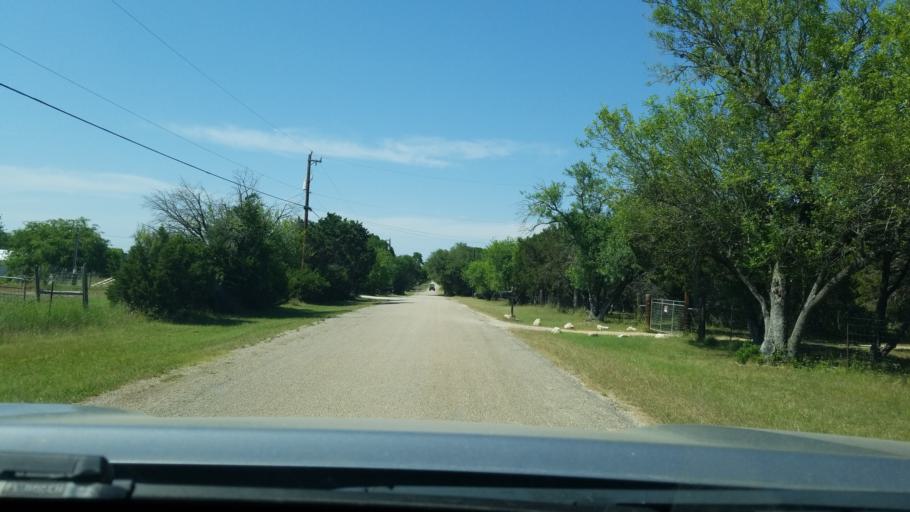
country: US
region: Texas
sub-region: Bexar County
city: Timberwood Park
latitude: 29.7476
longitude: -98.5179
